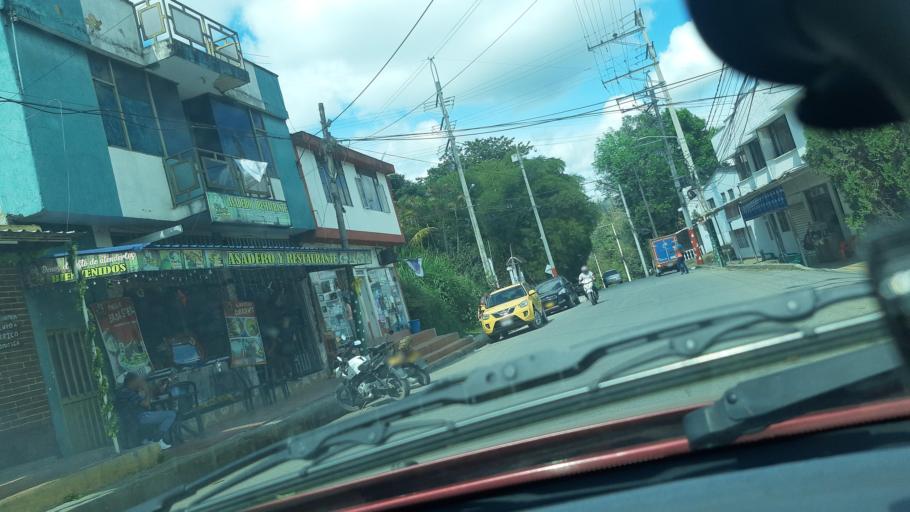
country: CO
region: Boyaca
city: Moniquira
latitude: 5.8695
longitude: -73.5742
